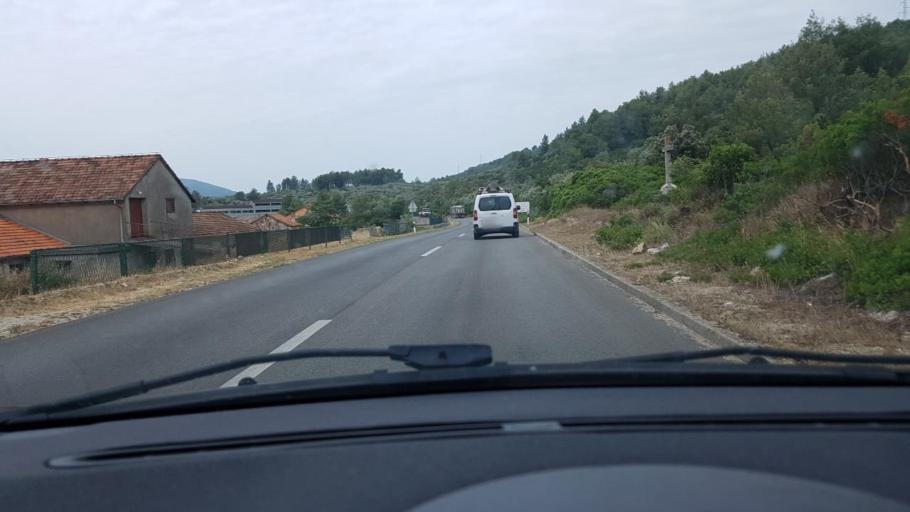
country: HR
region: Dubrovacko-Neretvanska
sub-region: Grad Dubrovnik
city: Vela Luka
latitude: 42.9478
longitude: 16.7734
